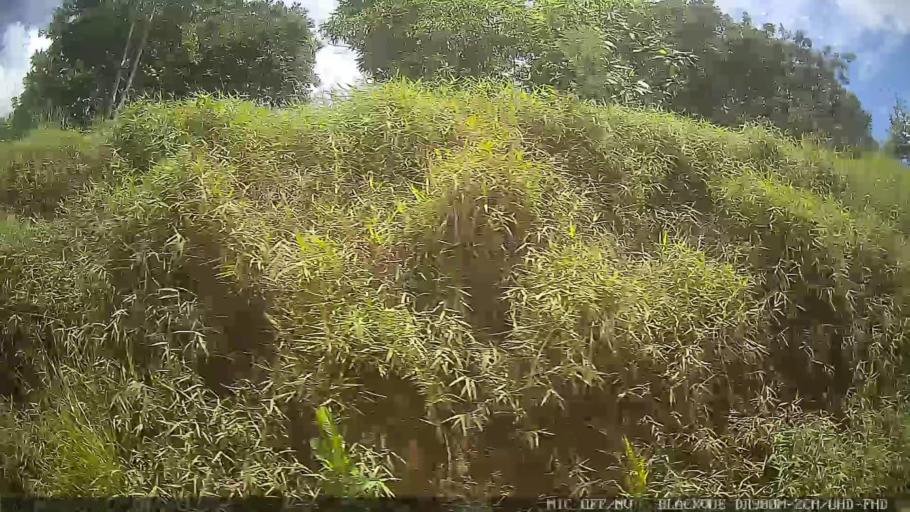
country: BR
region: Minas Gerais
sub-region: Extrema
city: Extrema
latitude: -22.7260
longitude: -46.3935
